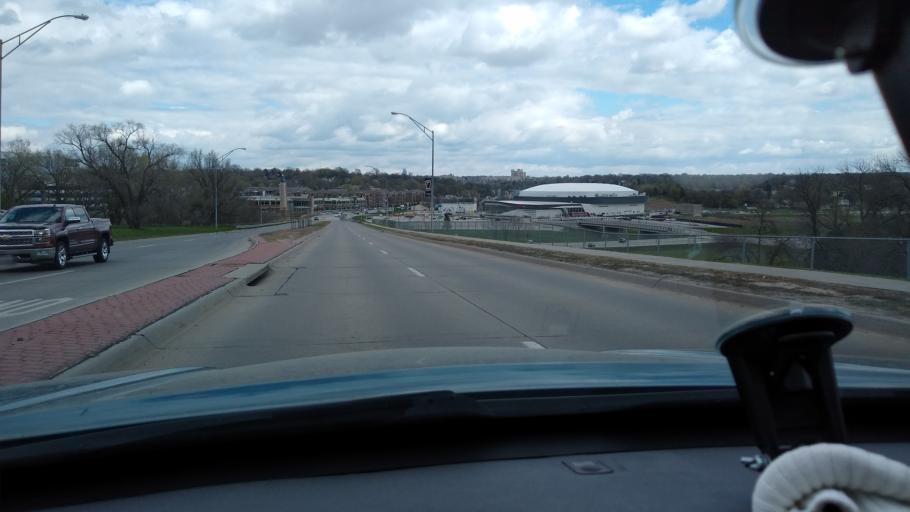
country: US
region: Nebraska
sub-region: Douglas County
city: Ralston
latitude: 41.2354
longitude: -96.0204
